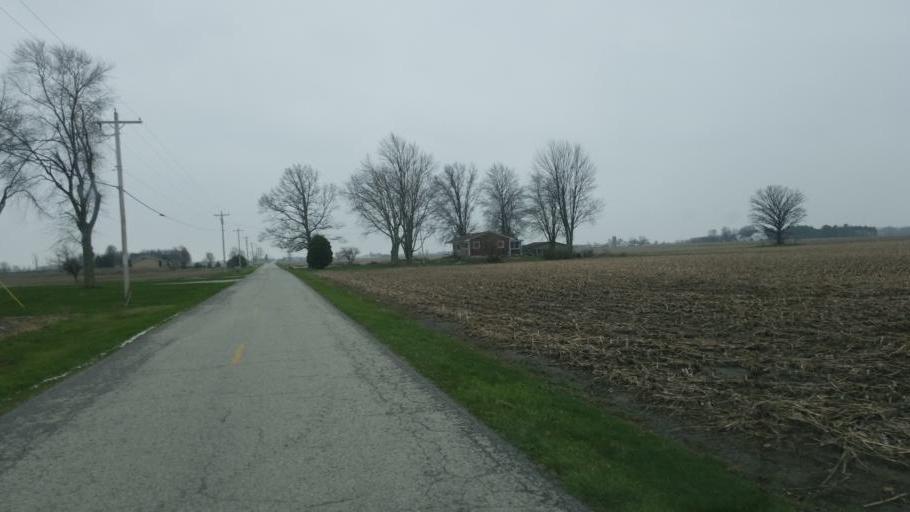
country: US
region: Ohio
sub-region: Marion County
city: Prospect
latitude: 40.4083
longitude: -83.1163
